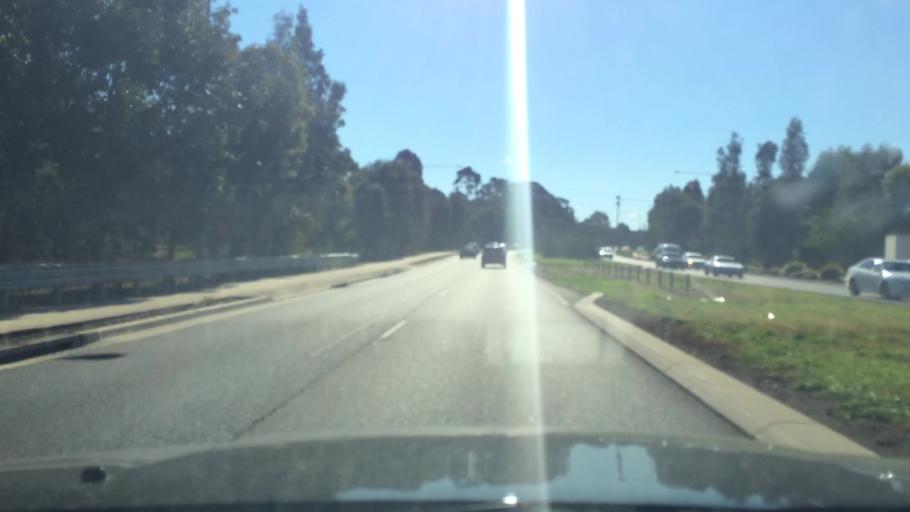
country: AU
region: New South Wales
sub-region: Liverpool
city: Miller
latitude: -33.9120
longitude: 150.8554
